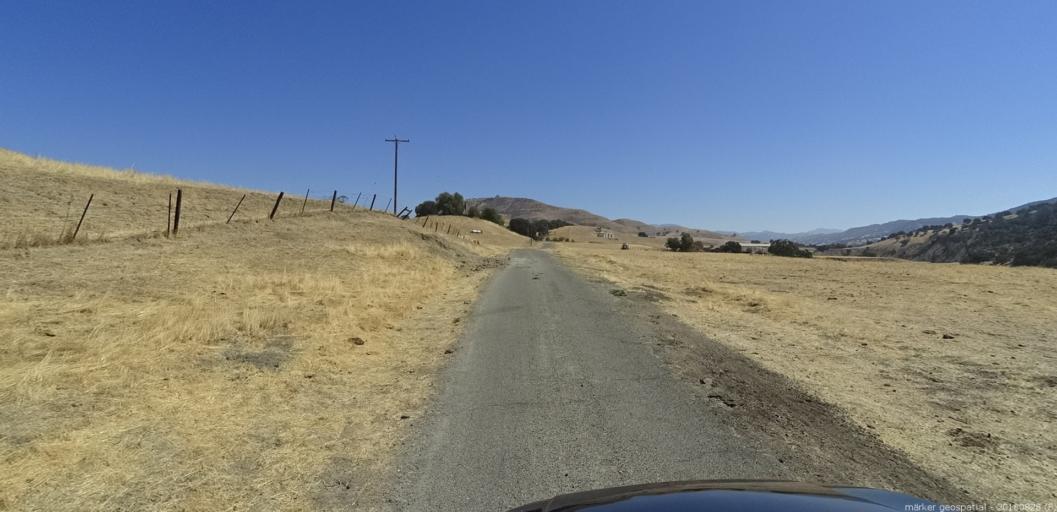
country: US
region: California
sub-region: San Luis Obispo County
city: San Miguel
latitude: 36.0652
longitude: -120.7882
